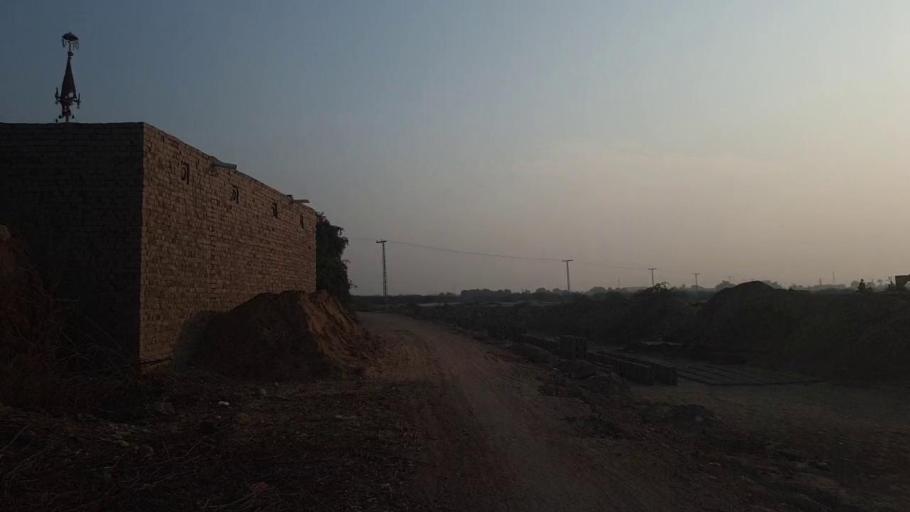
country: PK
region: Sindh
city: Bhit Shah
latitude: 25.7948
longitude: 68.4680
